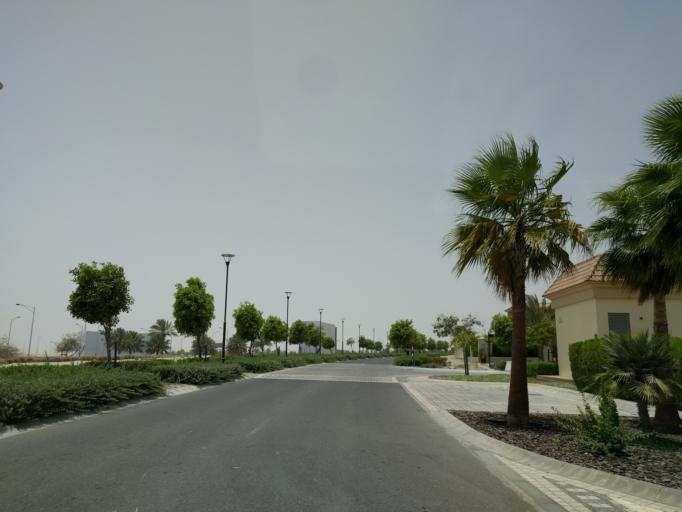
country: AE
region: Abu Dhabi
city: Abu Dhabi
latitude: 24.5490
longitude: 54.4510
